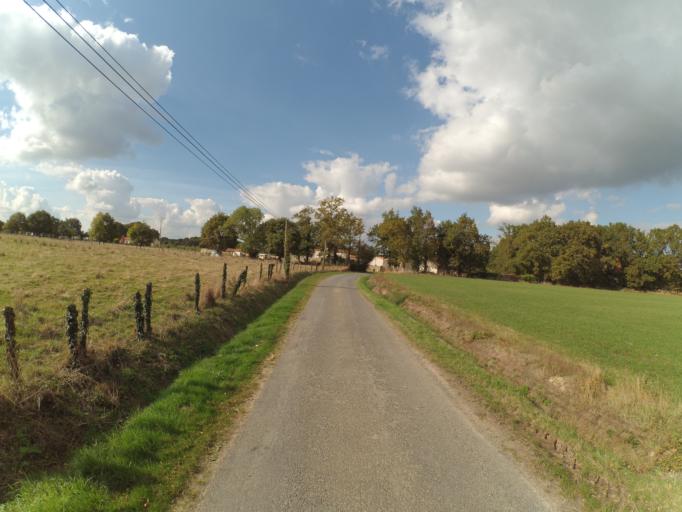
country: FR
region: Pays de la Loire
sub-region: Departement de la Loire-Atlantique
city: Remouille
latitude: 47.0685
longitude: -1.3562
